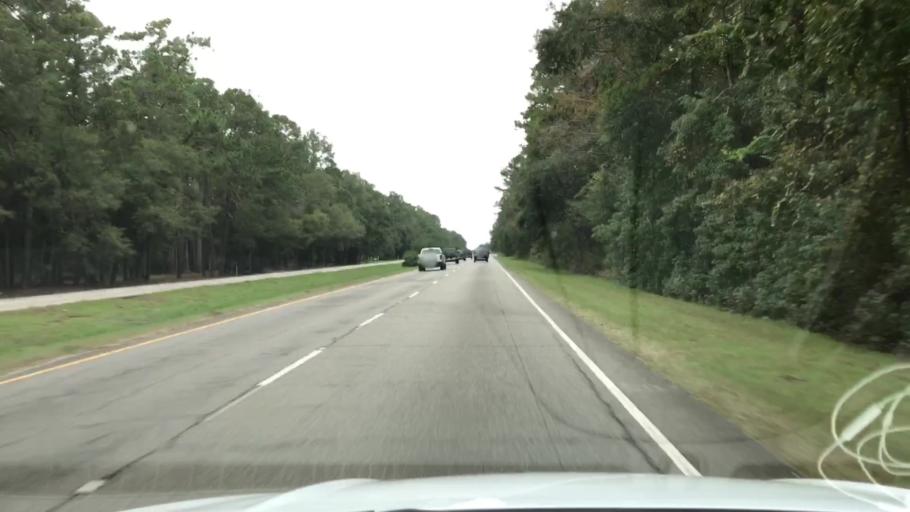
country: US
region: South Carolina
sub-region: Georgetown County
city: Murrells Inlet
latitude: 33.5183
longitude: -79.0700
